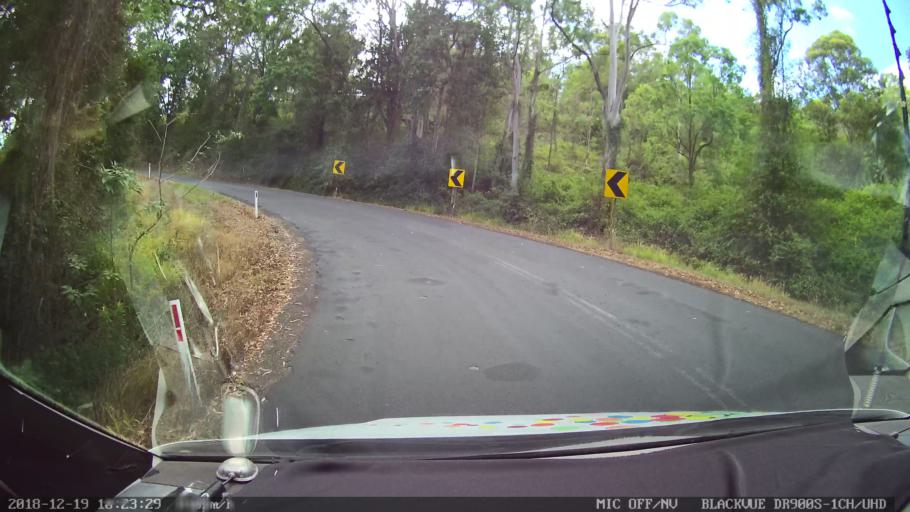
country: AU
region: New South Wales
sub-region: Lismore Municipality
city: Larnook
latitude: -28.5957
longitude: 153.0731
